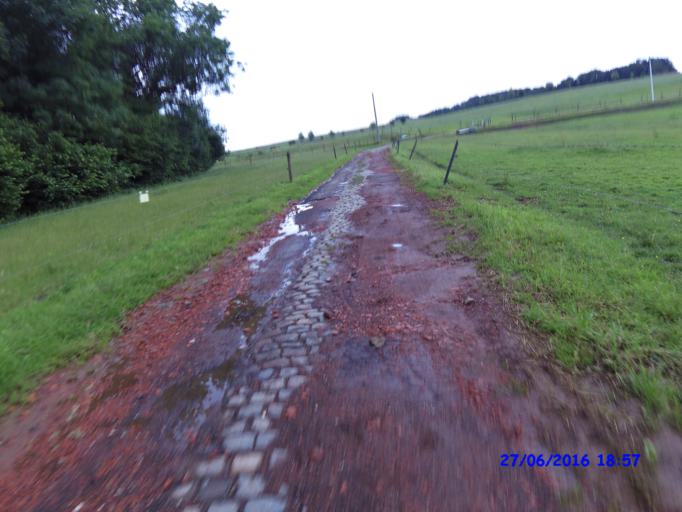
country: BE
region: Flanders
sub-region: Provincie Vlaams-Brabant
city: Wemmel
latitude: 50.8886
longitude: 4.2845
